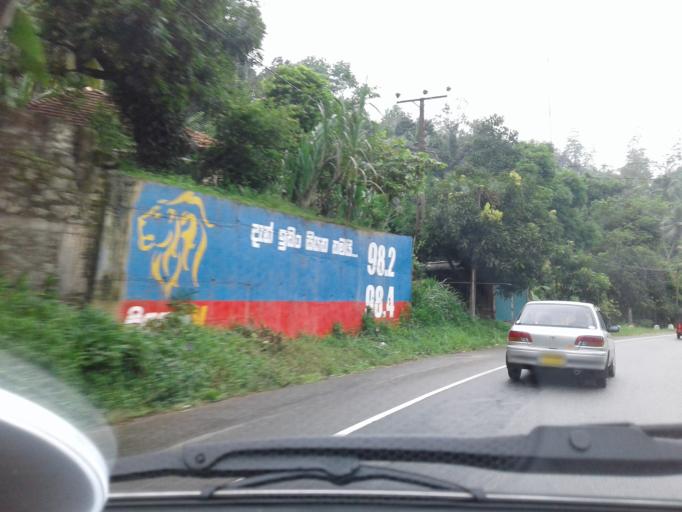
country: LK
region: Central
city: Kadugannawa
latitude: 7.2353
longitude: 80.2679
